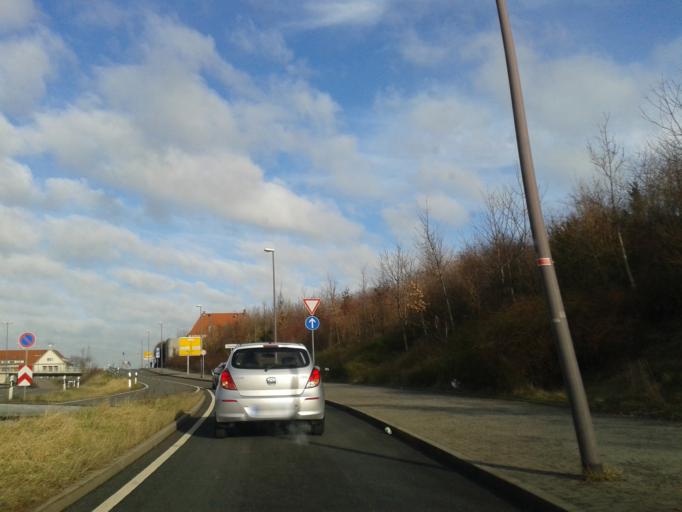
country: DE
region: Saxony
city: Bannewitz
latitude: 51.0175
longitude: 13.7296
